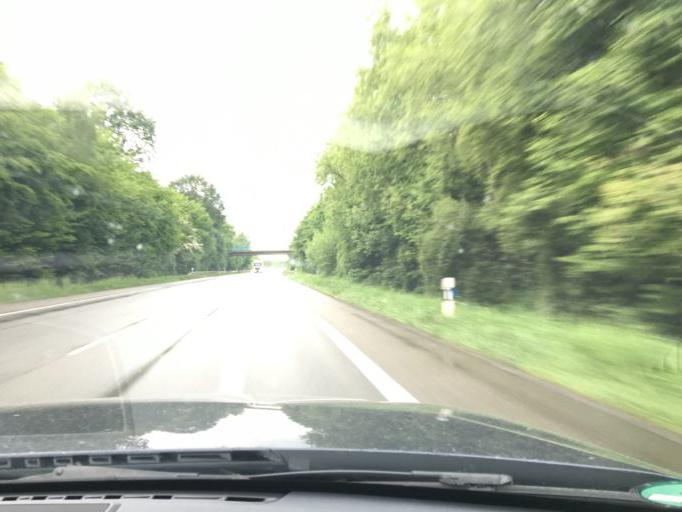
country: DE
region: North Rhine-Westphalia
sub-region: Regierungsbezirk Munster
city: Greven
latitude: 52.1164
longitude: 7.6023
